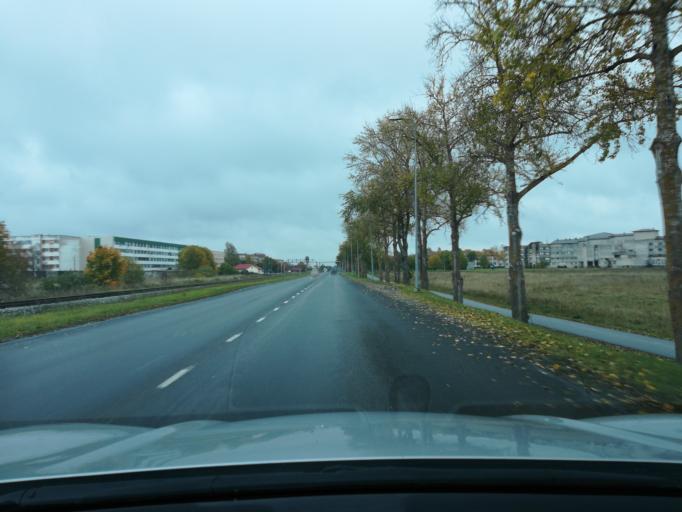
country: EE
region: Ida-Virumaa
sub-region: Johvi vald
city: Johvi
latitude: 59.3330
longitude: 27.4090
